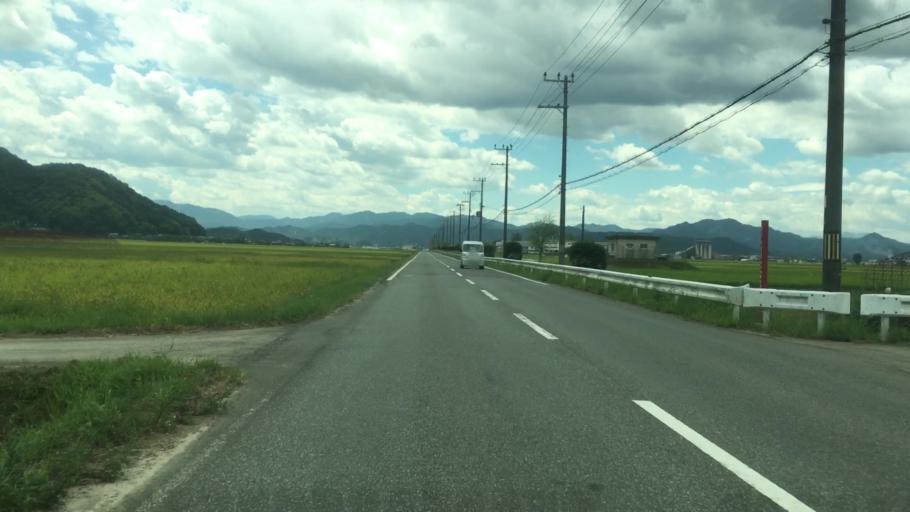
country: JP
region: Hyogo
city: Toyooka
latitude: 35.5382
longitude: 134.8397
